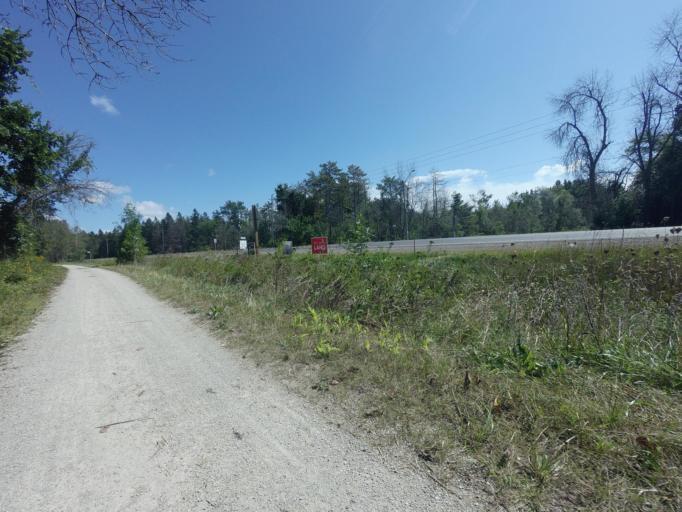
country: CA
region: Ontario
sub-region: Wellington County
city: Guelph
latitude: 43.7378
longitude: -80.3165
